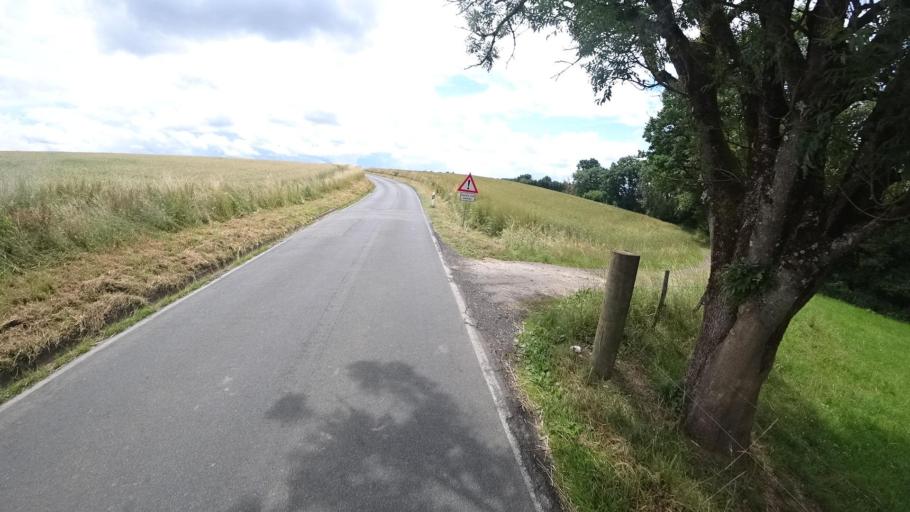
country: DE
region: Rheinland-Pfalz
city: Fiersbach
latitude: 50.6942
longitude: 7.4998
